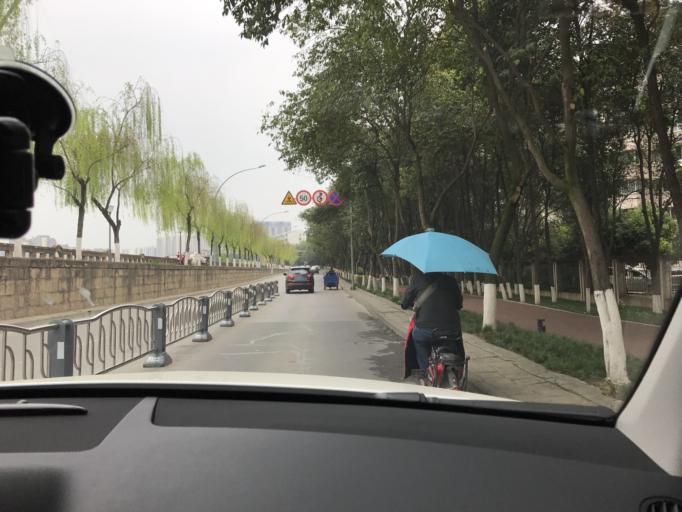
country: CN
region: Sichuan
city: Mianyang
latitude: 31.4565
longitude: 104.7064
